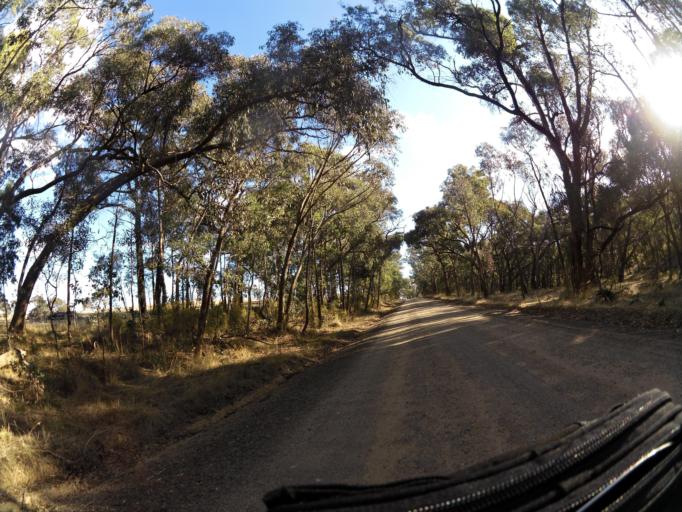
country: AU
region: Victoria
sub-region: Greater Bendigo
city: Kennington
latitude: -37.0205
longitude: 144.8033
